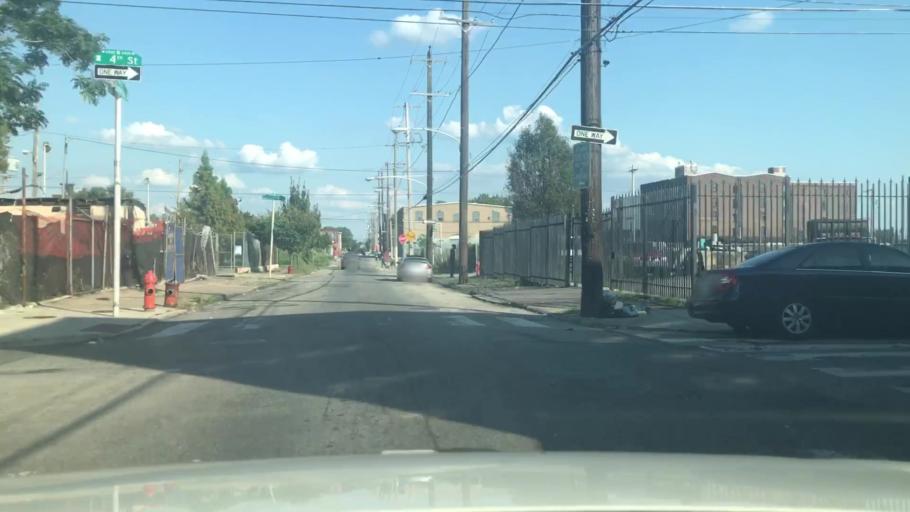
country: US
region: Pennsylvania
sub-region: Philadelphia County
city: Philadelphia
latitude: 39.9888
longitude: -75.1391
